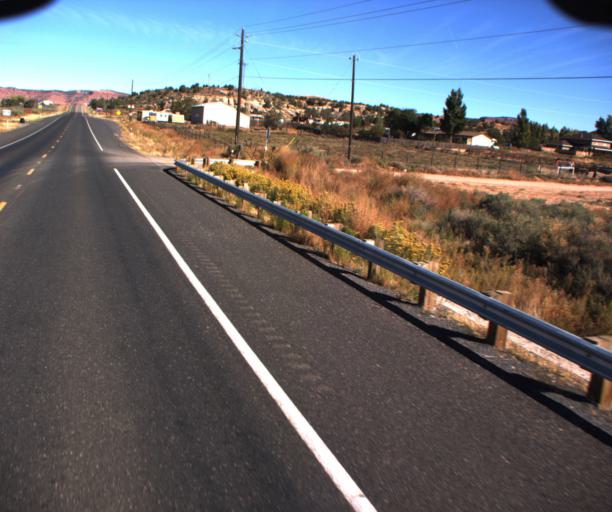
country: US
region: Utah
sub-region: Kane County
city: Kanab
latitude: 36.9972
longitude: -112.5302
